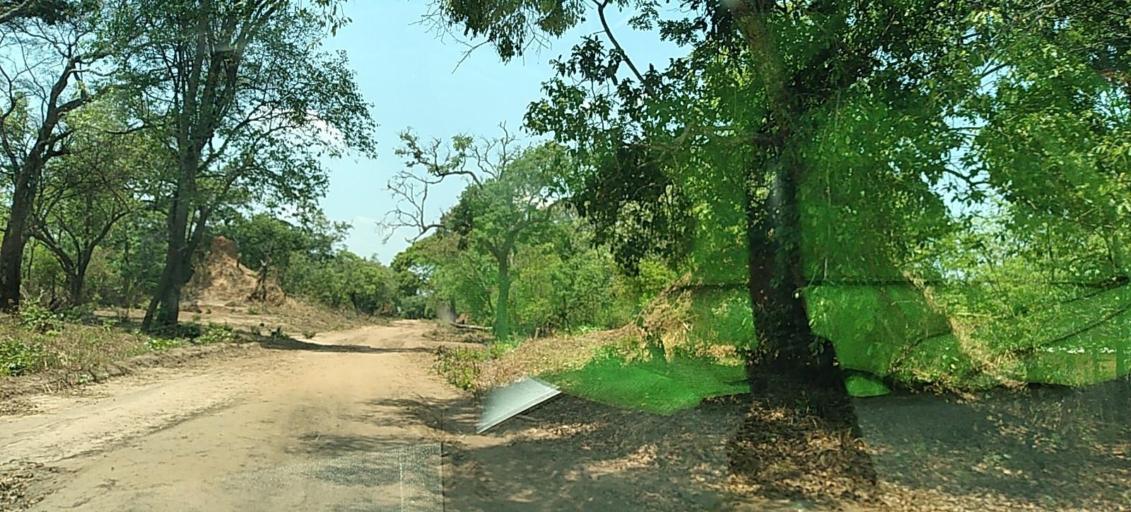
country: CD
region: Katanga
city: Kolwezi
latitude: -11.3196
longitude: 25.2309
